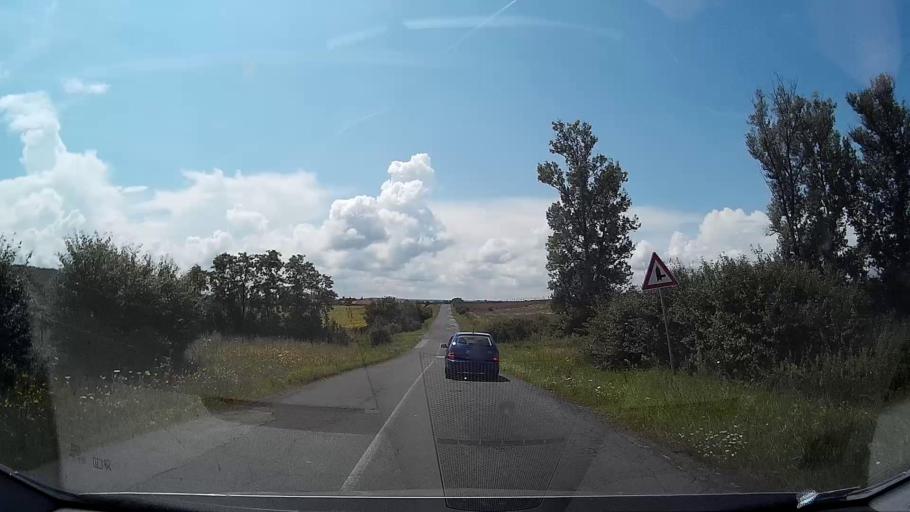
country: SK
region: Banskobystricky
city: Fil'akovo
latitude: 48.3331
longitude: 19.8201
